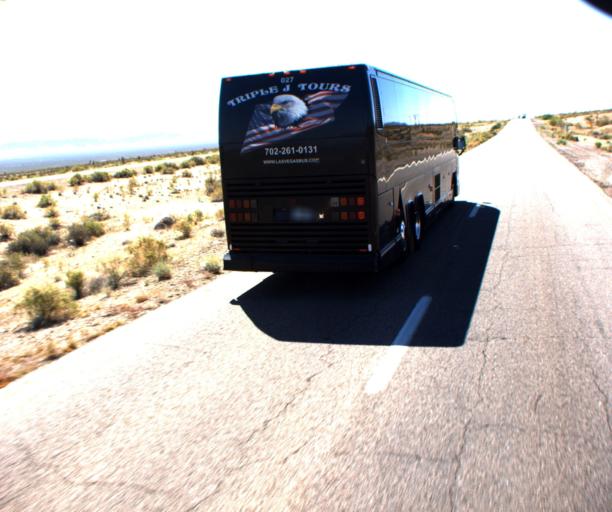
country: US
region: Arizona
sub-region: Mohave County
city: Dolan Springs
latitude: 35.7613
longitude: -114.5080
